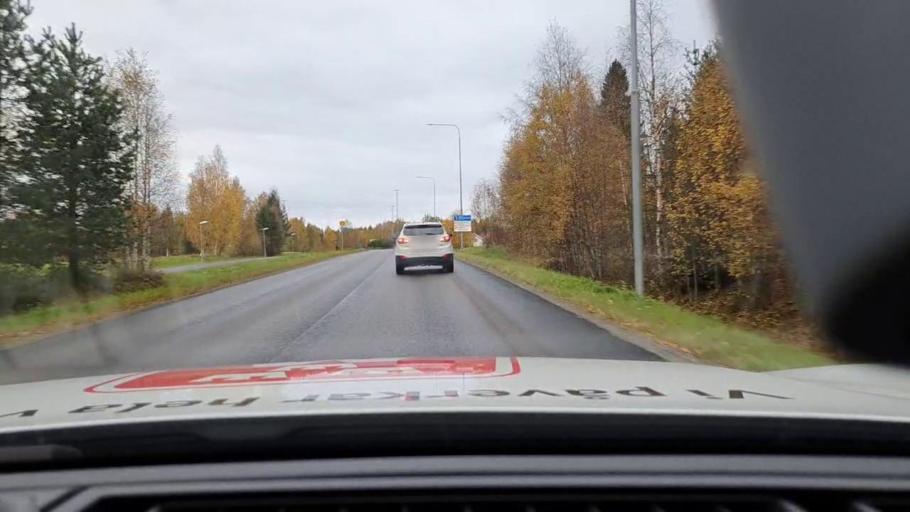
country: SE
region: Norrbotten
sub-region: Bodens Kommun
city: Saevast
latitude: 65.7640
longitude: 21.7388
